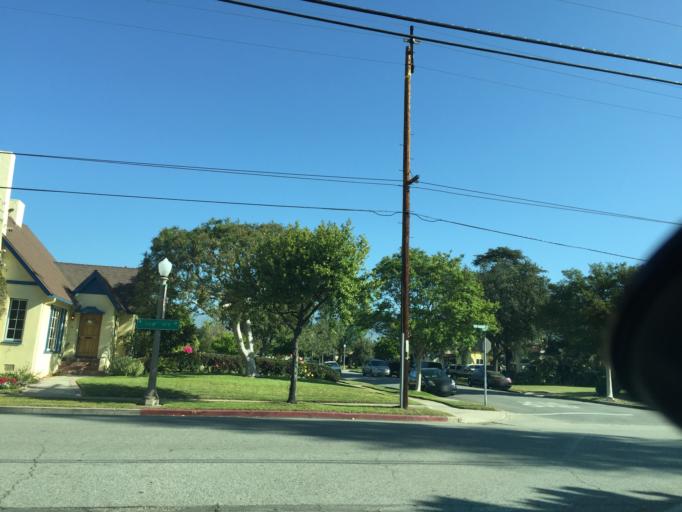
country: US
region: California
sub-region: Los Angeles County
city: Alhambra
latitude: 34.0826
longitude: -118.1243
